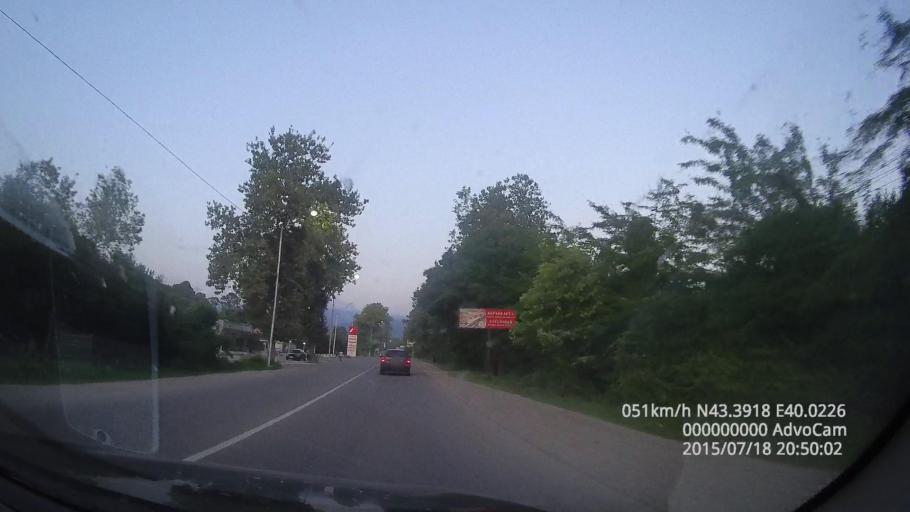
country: GE
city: Gantiadi
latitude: 43.3916
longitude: 40.0239
